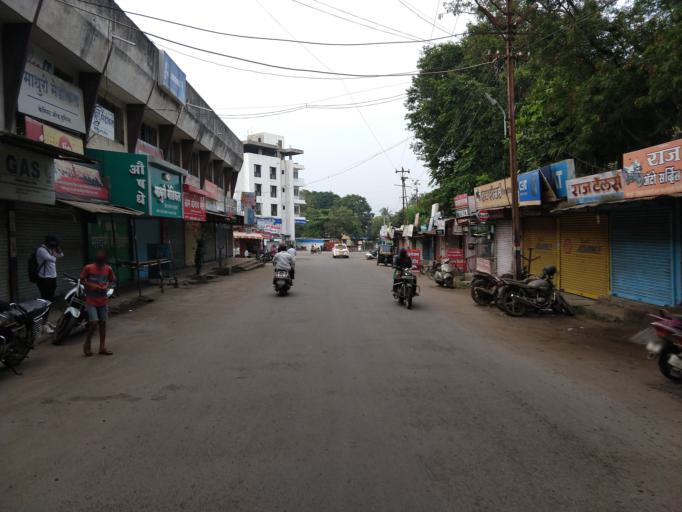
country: IN
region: Maharashtra
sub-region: Pune Division
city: Sasvad
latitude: 18.3470
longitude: 74.0285
